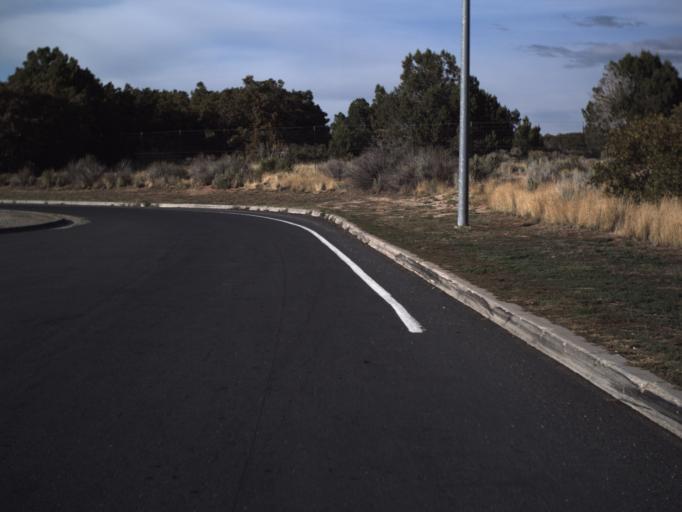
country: US
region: Utah
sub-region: Iron County
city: Cedar City
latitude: 37.5136
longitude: -113.2105
